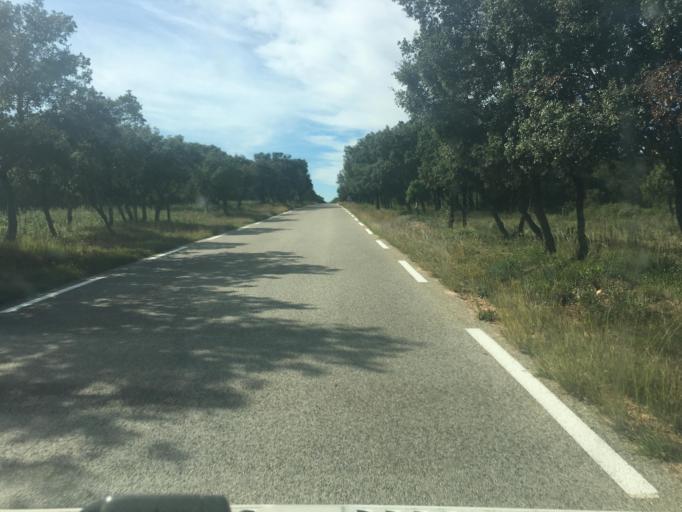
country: FR
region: Languedoc-Roussillon
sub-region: Departement du Gard
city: Saint-Quentin-la-Poterie
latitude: 44.0316
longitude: 4.5150
